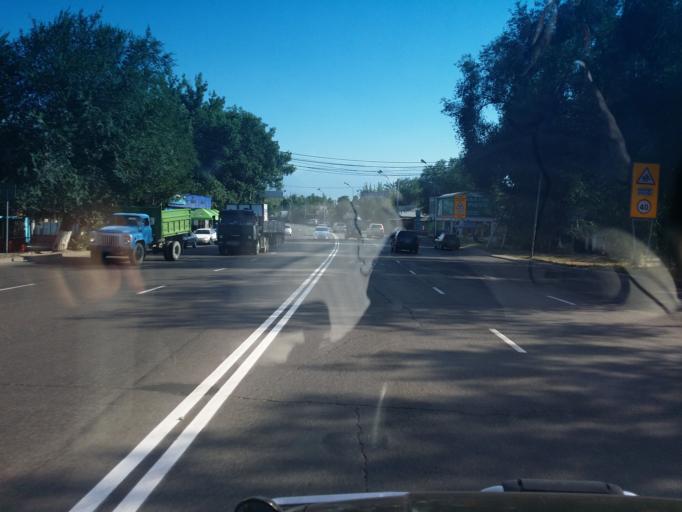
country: KZ
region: Almaty Oblysy
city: Pervomayskiy
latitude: 43.3446
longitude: 76.9325
